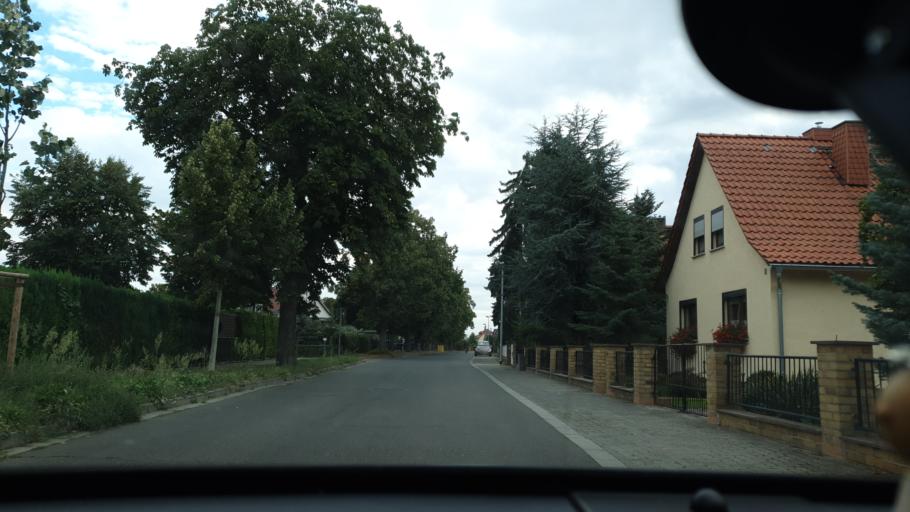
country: DE
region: Saxony
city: Torgau
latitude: 51.5537
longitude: 12.9938
